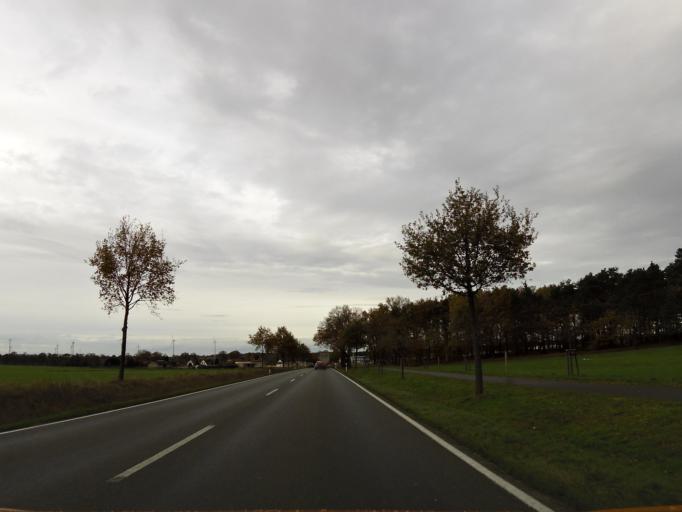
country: DE
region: Saxony-Anhalt
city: Kalbe
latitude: 52.6559
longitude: 11.2885
